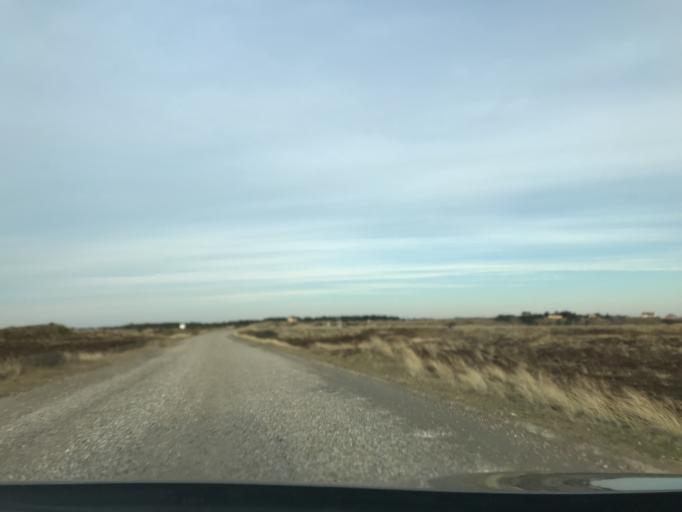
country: DK
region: Central Jutland
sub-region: Ringkobing-Skjern Kommune
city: Hvide Sande
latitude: 55.8179
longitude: 8.1791
